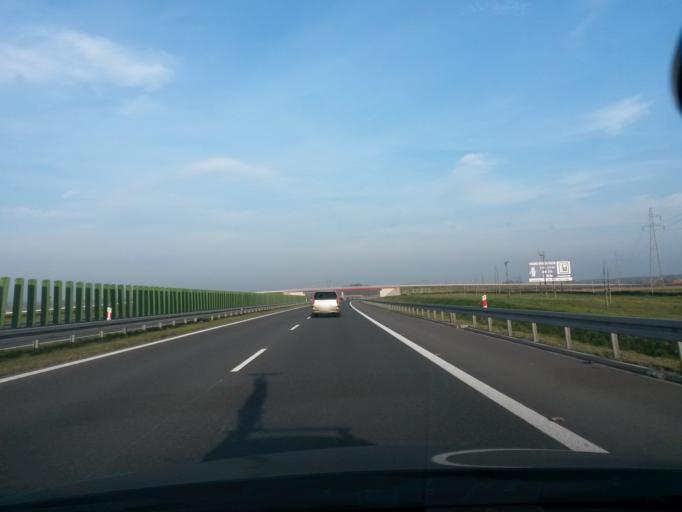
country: PL
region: Lower Silesian Voivodeship
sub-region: Powiat wroclawski
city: Mirkow
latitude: 51.2129
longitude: 17.1324
